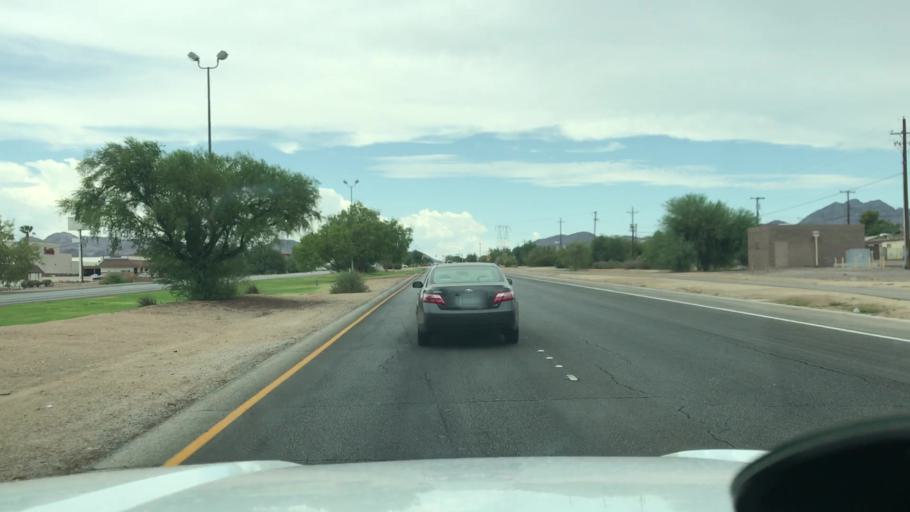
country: US
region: Nevada
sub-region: Clark County
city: Henderson
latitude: 36.0279
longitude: -114.9691
